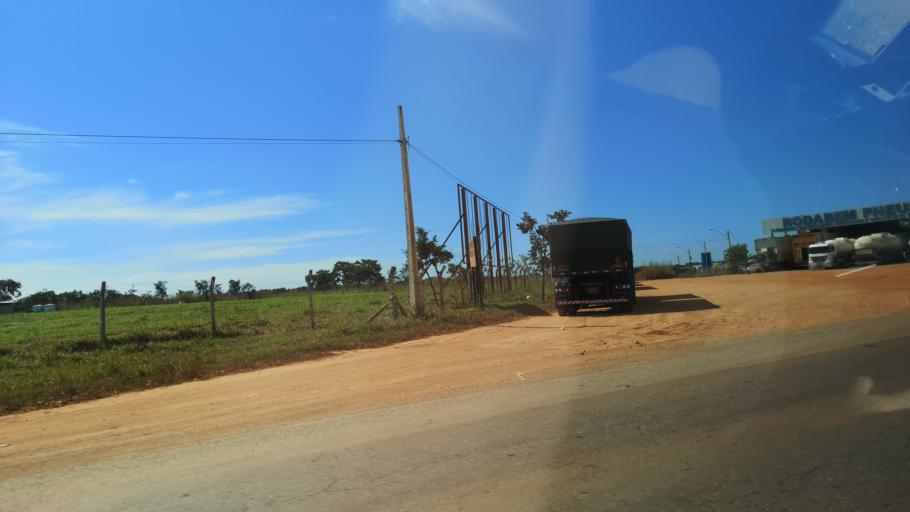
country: BR
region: Goias
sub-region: Senador Canedo
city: Senador Canedo
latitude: -16.7169
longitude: -49.1093
